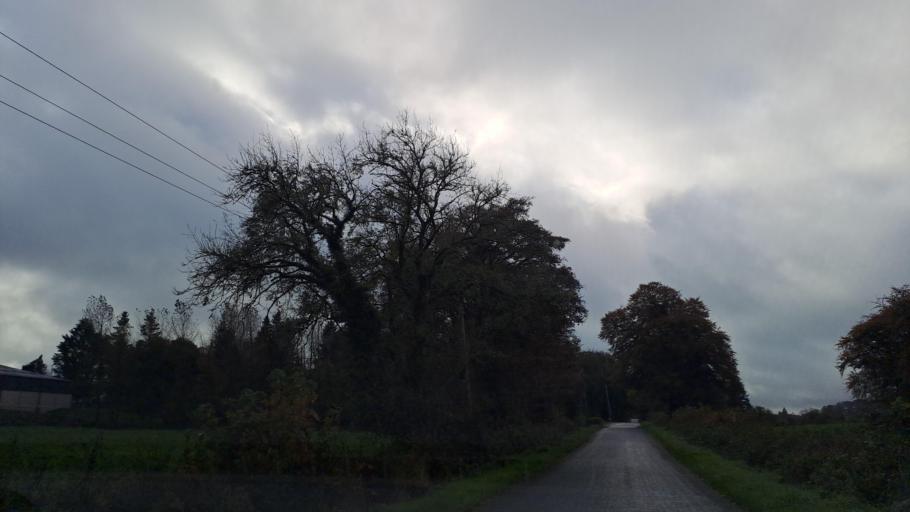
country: IE
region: Ulster
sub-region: An Cabhan
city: Bailieborough
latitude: 53.9690
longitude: -6.9869
